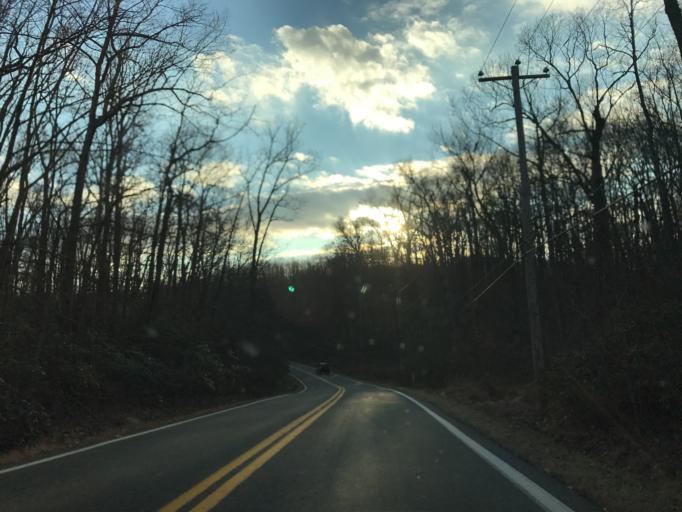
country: US
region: Maryland
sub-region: Cecil County
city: Charlestown
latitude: 39.4914
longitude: -75.9774
